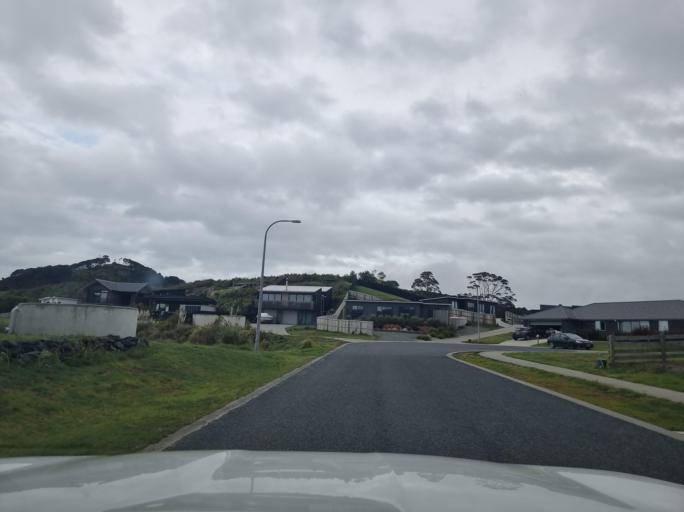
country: NZ
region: Auckland
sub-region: Auckland
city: Wellsford
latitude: -36.0919
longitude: 174.5770
